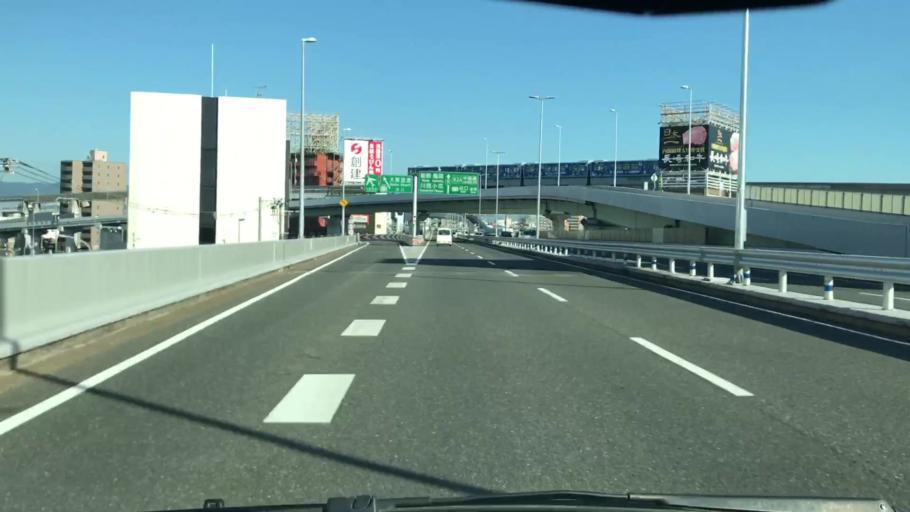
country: JP
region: Osaka
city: Toyonaka
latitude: 34.7881
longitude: 135.4484
